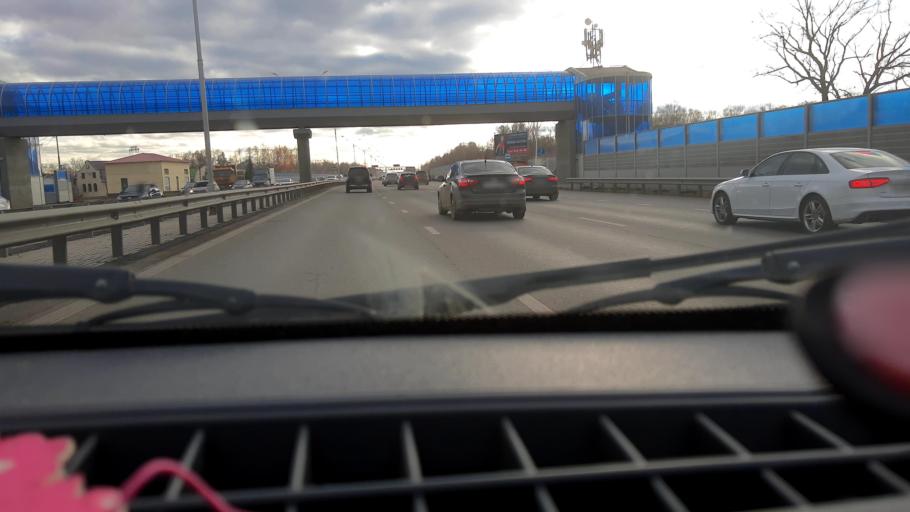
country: RU
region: Bashkortostan
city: Ufa
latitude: 54.6963
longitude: 55.9403
